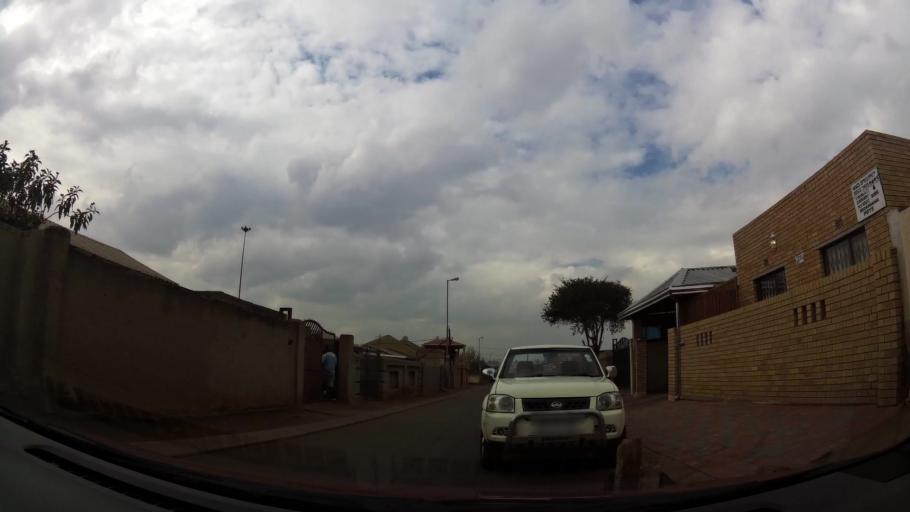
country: ZA
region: Gauteng
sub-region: City of Johannesburg Metropolitan Municipality
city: Soweto
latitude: -26.2582
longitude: 27.8346
